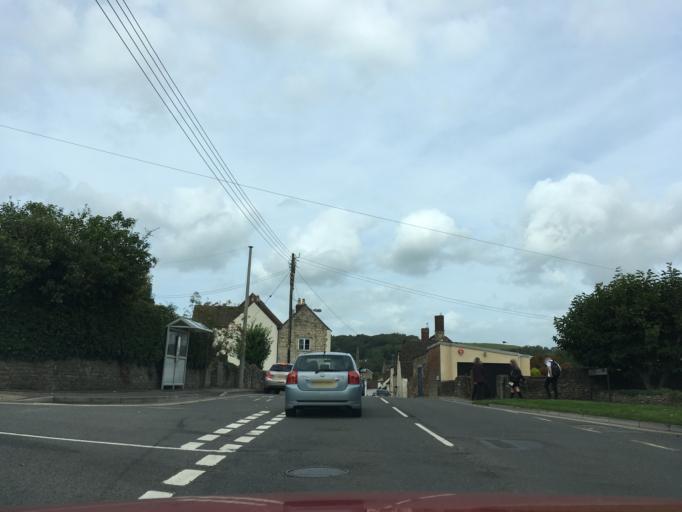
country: GB
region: England
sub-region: Gloucestershire
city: Wotton-under-Edge
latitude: 51.6366
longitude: -2.3561
